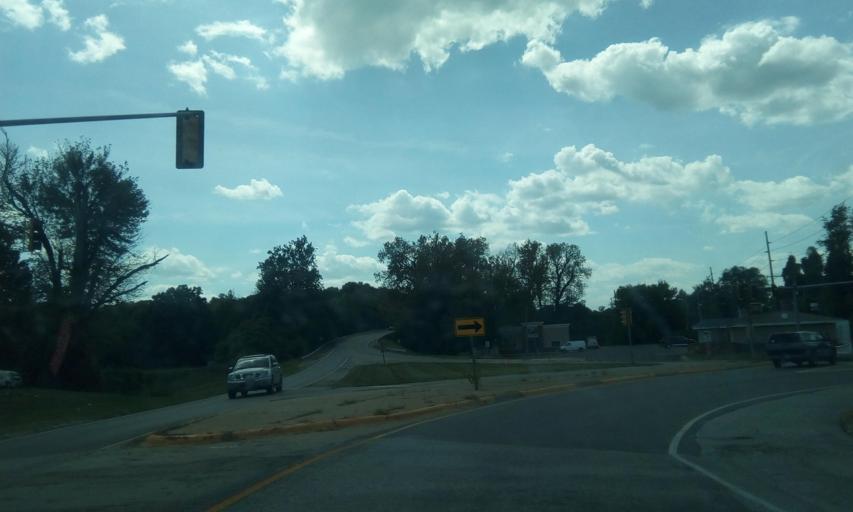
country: US
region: Illinois
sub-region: Saint Clair County
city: Caseyville
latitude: 38.6458
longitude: -90.0164
